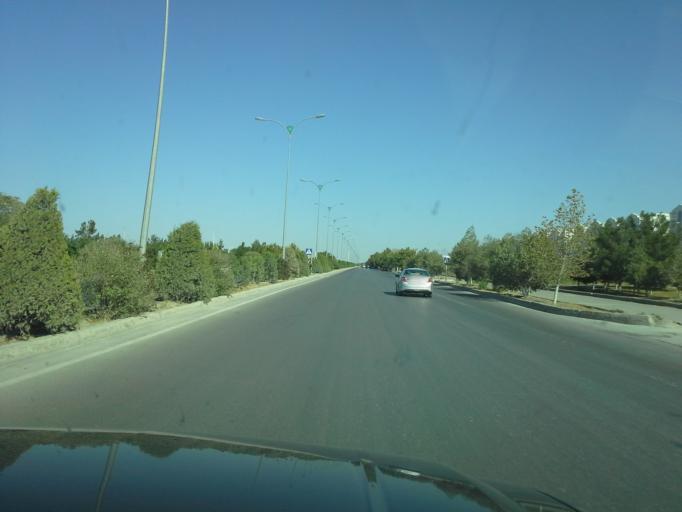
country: TM
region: Ahal
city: Abadan
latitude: 38.1655
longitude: 57.9352
